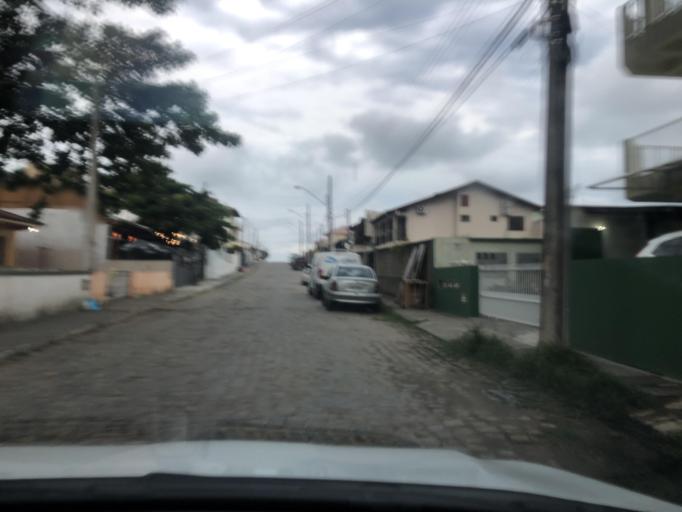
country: BR
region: Santa Catarina
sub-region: Sao Francisco Do Sul
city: Sao Francisco do Sul
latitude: -26.2296
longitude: -48.5022
